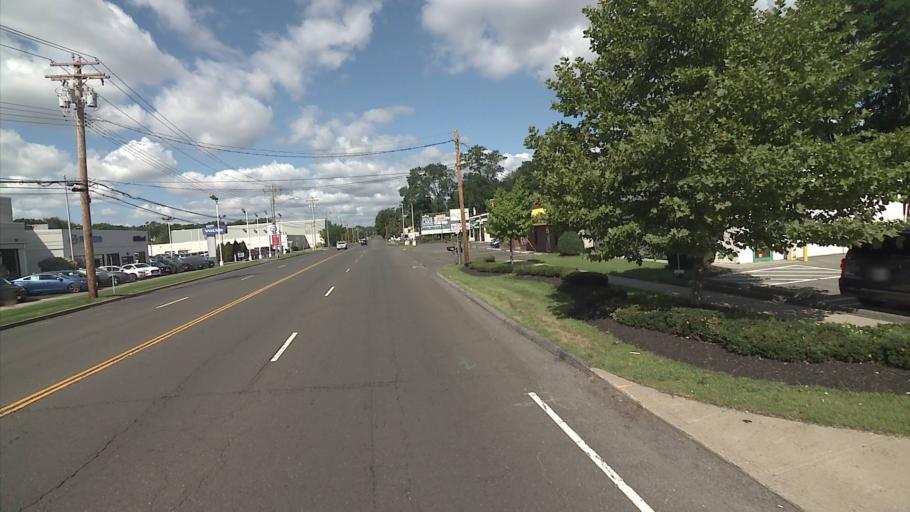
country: US
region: Connecticut
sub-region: New Haven County
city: Milford
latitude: 41.2319
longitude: -73.0500
